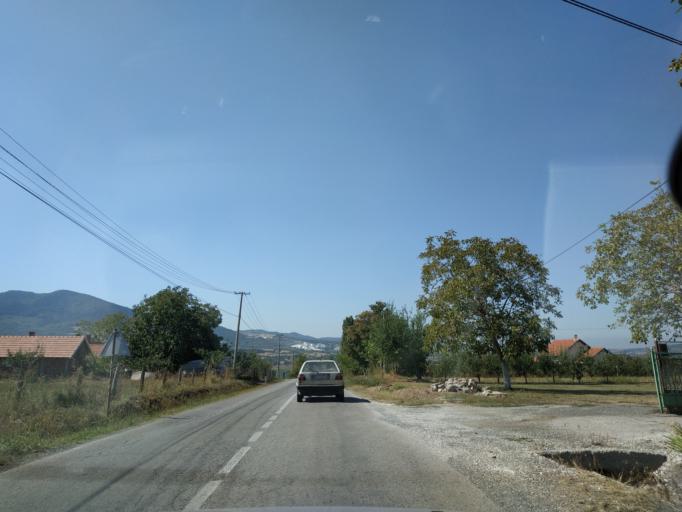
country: RS
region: Central Serbia
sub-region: Sumadijski Okrug
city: Topola
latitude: 44.2732
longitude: 20.6352
